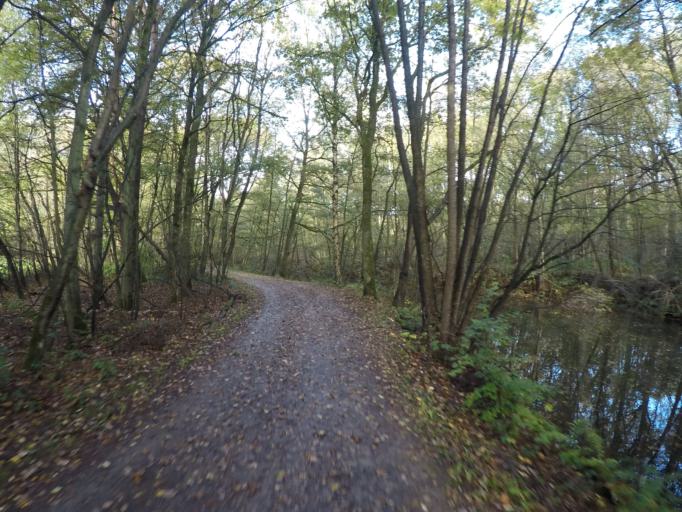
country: BE
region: Flanders
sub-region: Provincie Antwerpen
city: Schilde
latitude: 51.2385
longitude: 4.6068
